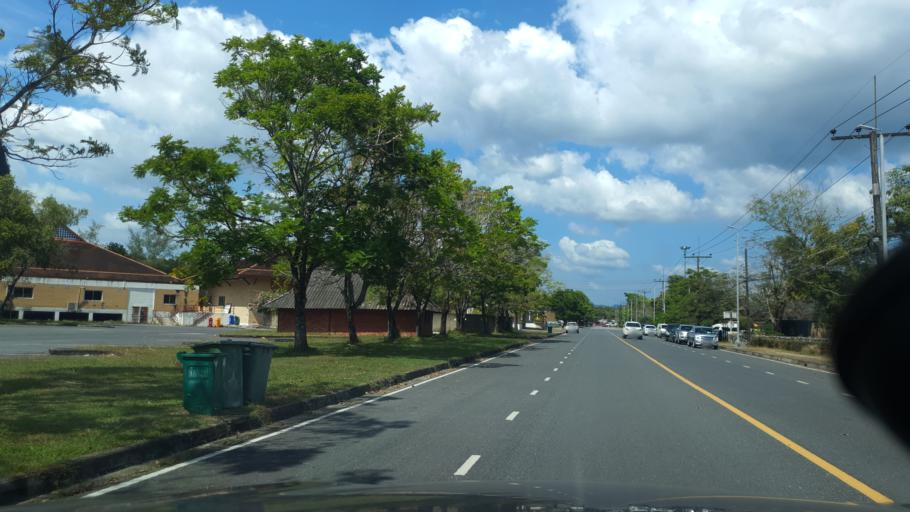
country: TH
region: Phangnga
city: Phang Nga
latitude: 8.3999
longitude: 98.5130
